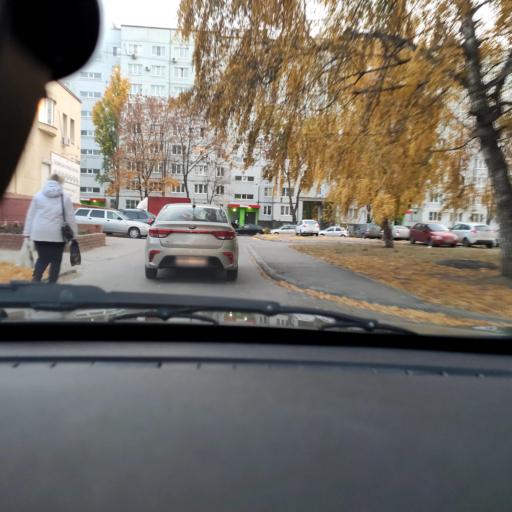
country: RU
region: Samara
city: Tol'yatti
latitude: 53.5338
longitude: 49.3170
